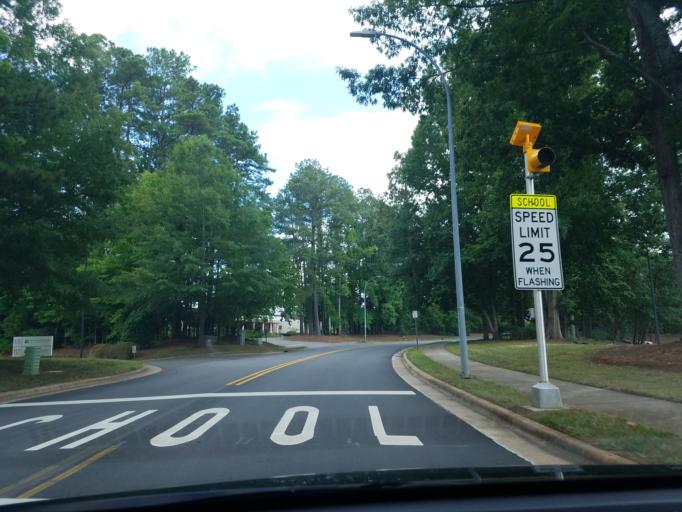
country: US
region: North Carolina
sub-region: Wake County
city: Apex
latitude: 35.7342
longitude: -78.8074
